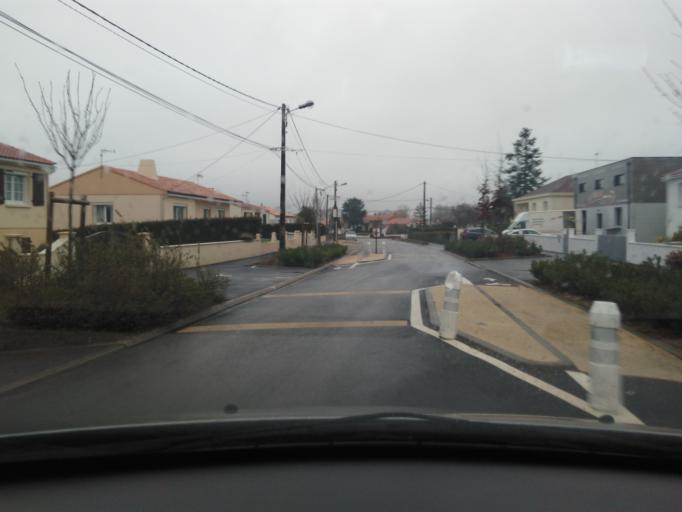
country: FR
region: Pays de la Loire
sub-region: Departement de la Vendee
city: La Ferriere
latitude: 46.7083
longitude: -1.3105
